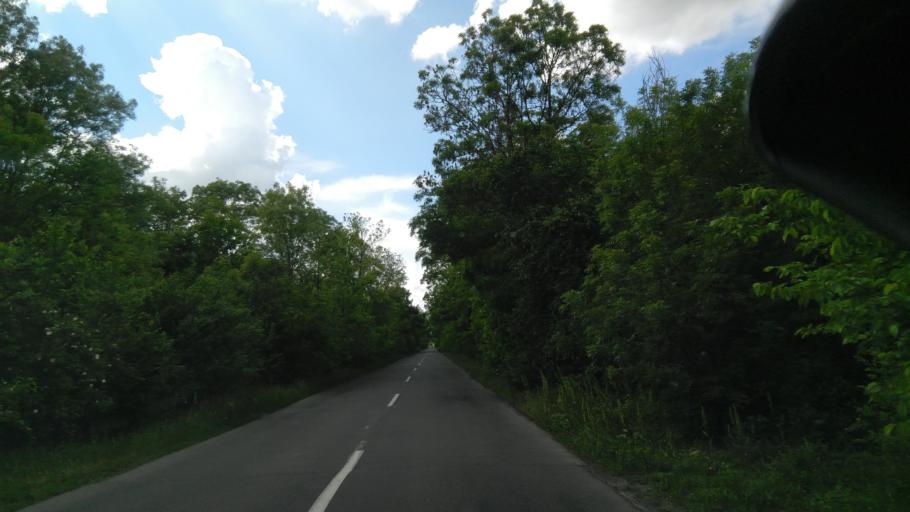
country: HU
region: Bekes
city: Bucsa
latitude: 47.1723
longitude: 21.0687
